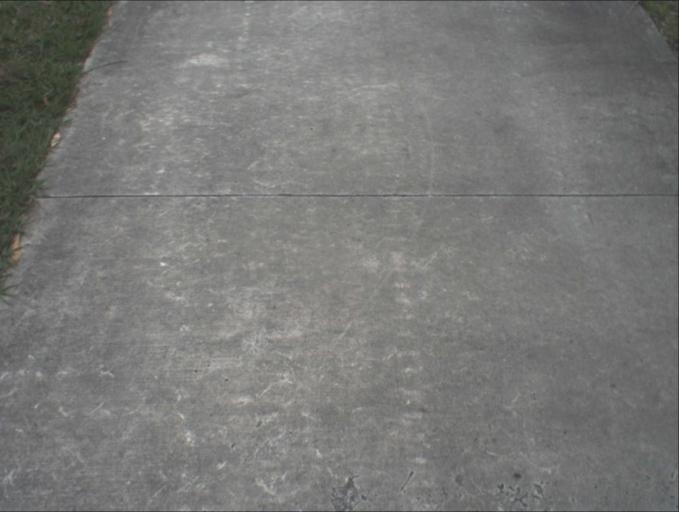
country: AU
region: Queensland
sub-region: Logan
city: Logan Reserve
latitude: -27.7047
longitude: 153.0758
